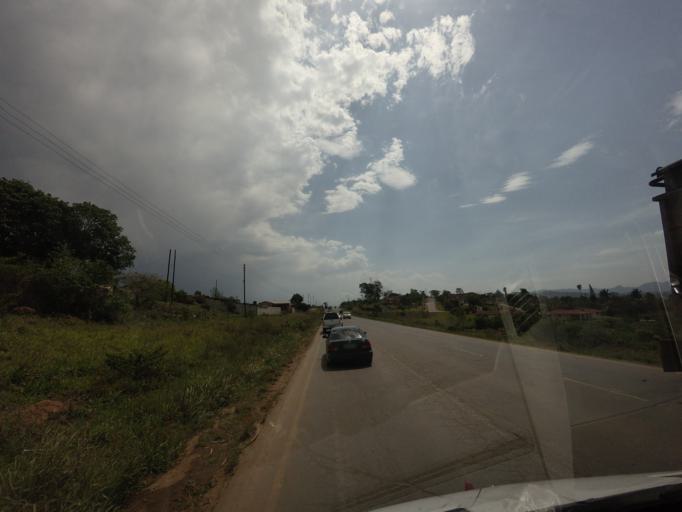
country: SZ
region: Manzini
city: Manzini
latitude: -26.4928
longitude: 31.4071
